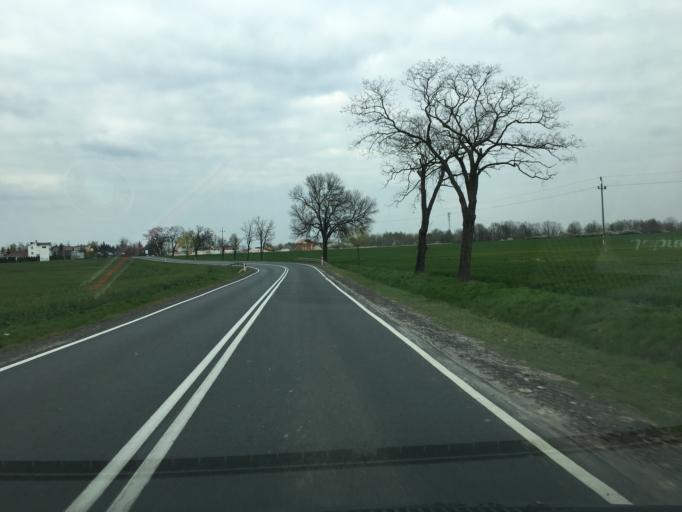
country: PL
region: Lower Silesian Voivodeship
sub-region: Powiat legnicki
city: Prochowice
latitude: 51.2670
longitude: 16.3457
